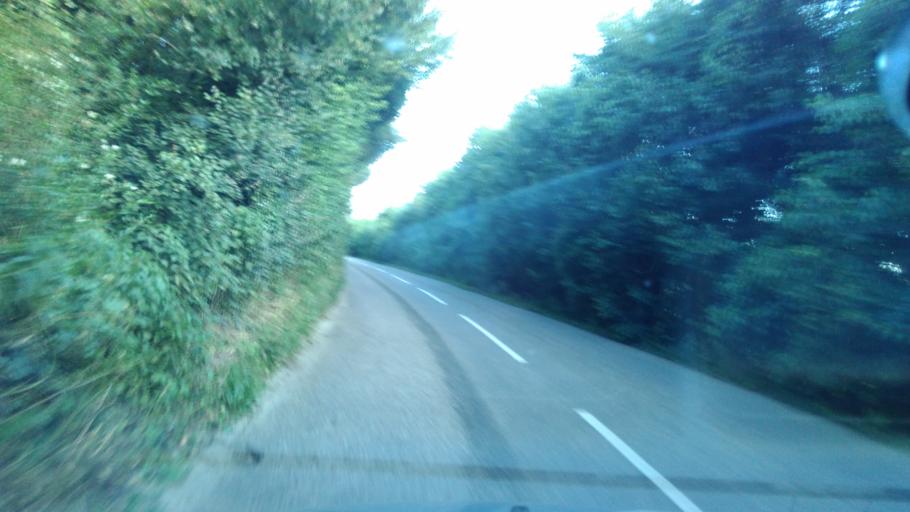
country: GB
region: England
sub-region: Kent
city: Dunkirk
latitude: 51.2530
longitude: 0.9578
